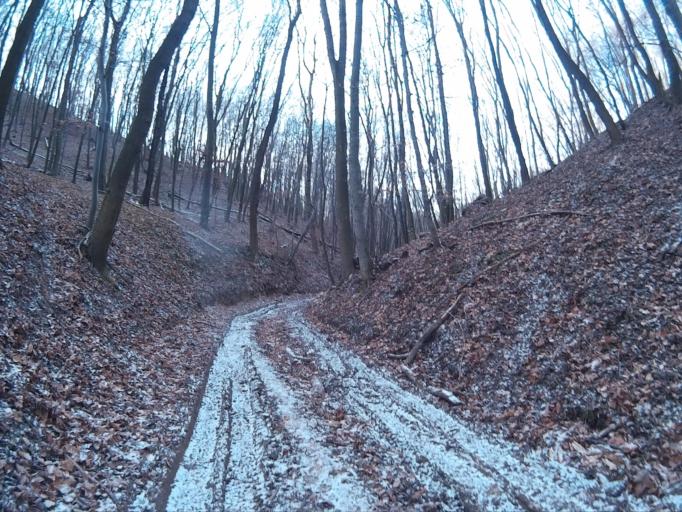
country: HU
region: Fejer
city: Szarliget
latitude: 47.5136
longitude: 18.4204
